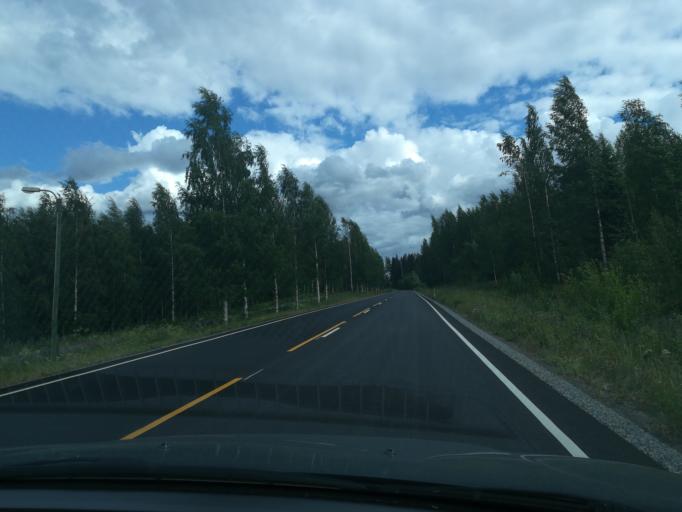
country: FI
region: Southern Savonia
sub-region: Mikkeli
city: Mikkeli
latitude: 61.6591
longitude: 27.1173
